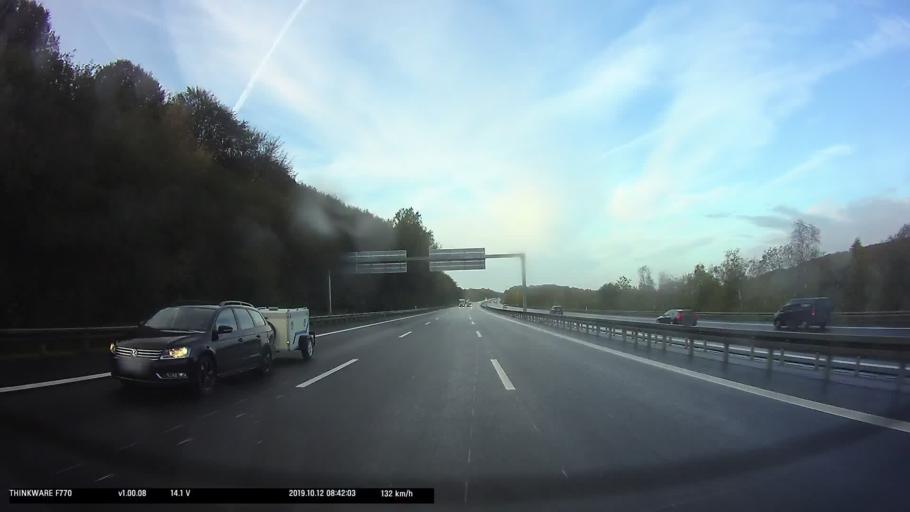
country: DK
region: Central Jutland
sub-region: Skanderborg Kommune
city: Skanderborg
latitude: 56.0547
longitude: 9.9490
